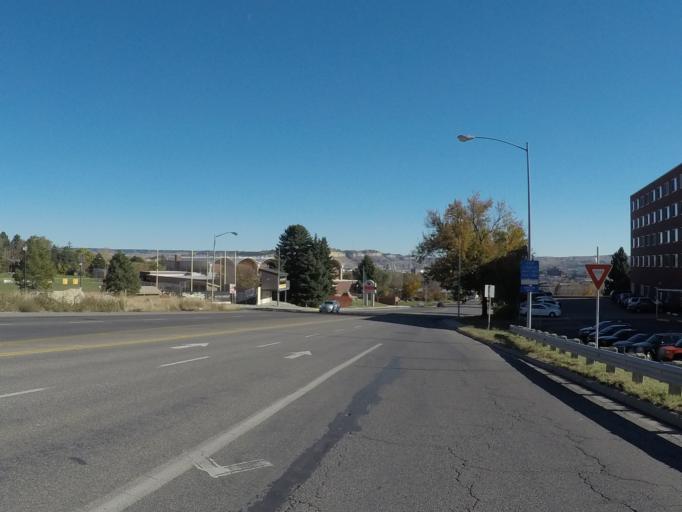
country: US
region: Montana
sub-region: Yellowstone County
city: Billings
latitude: 45.7983
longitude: -108.5202
